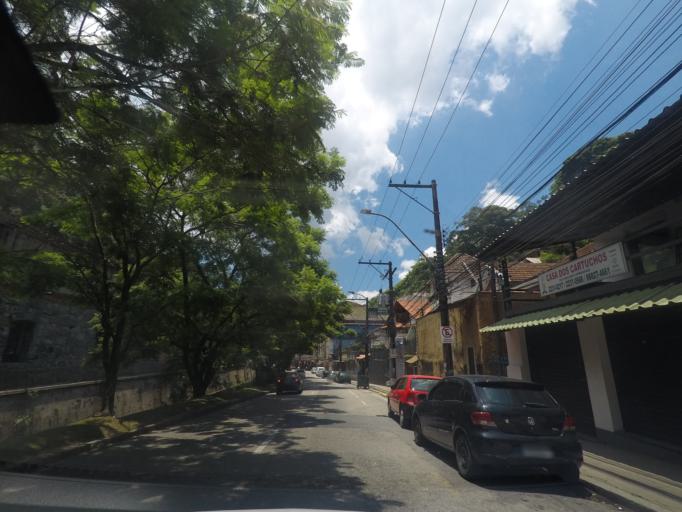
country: BR
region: Rio de Janeiro
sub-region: Petropolis
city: Petropolis
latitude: -22.5143
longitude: -43.1814
